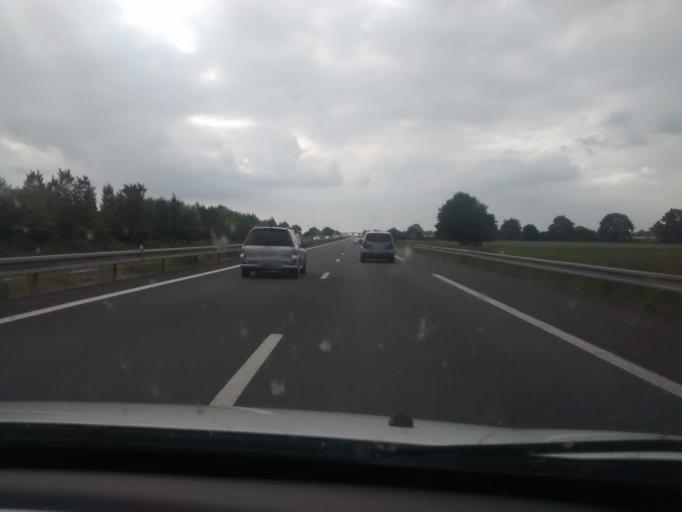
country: FR
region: Pays de la Loire
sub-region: Departement de la Sarthe
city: Brulon
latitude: 48.0120
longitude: -0.2973
